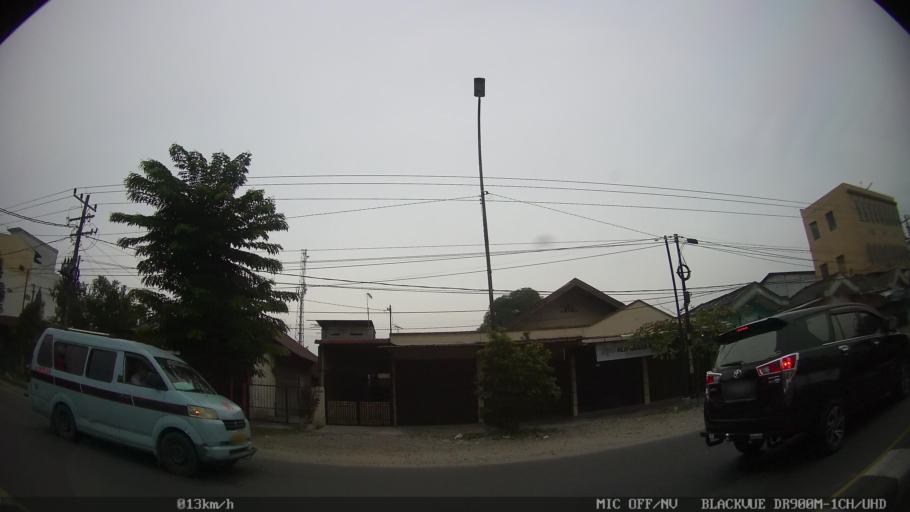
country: ID
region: North Sumatra
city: Medan
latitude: 3.5969
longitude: 98.7139
